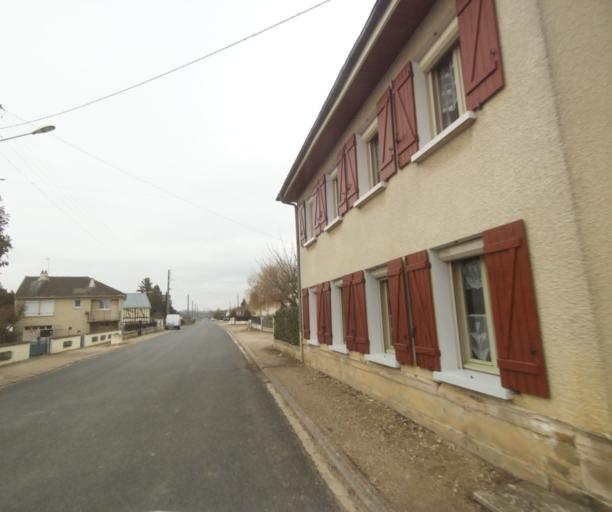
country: FR
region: Champagne-Ardenne
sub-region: Departement de la Haute-Marne
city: Villiers-en-Lieu
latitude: 48.6413
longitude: 4.8694
